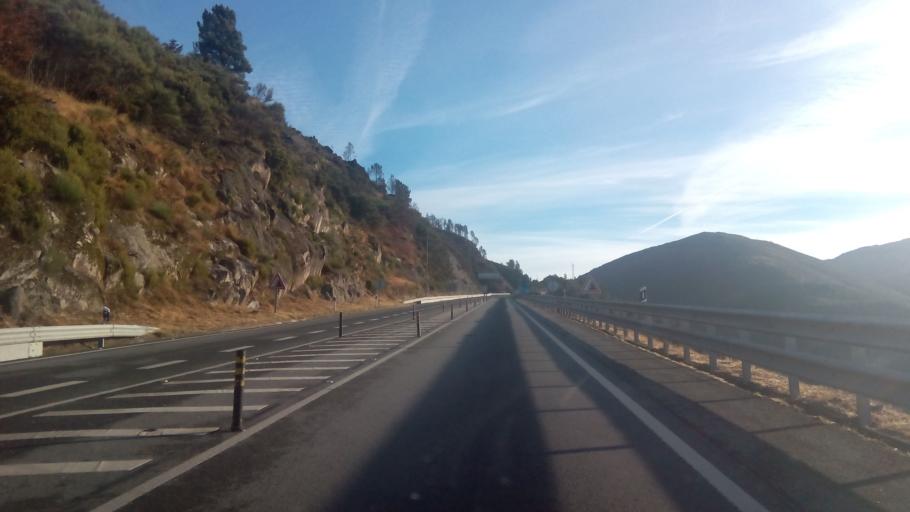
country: PT
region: Porto
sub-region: Baiao
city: Valadares
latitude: 41.2561
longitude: -7.9560
